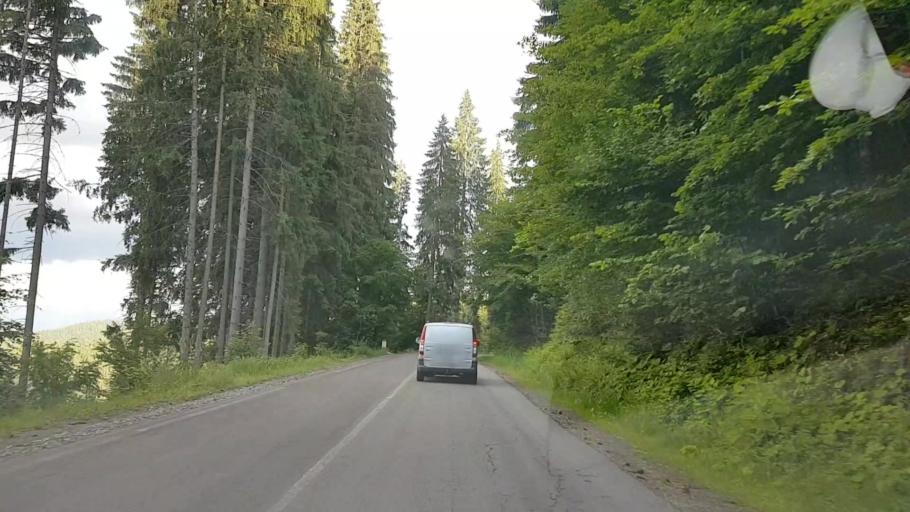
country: RO
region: Harghita
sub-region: Comuna Varsag
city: Varsag
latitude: 46.6672
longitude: 25.3193
